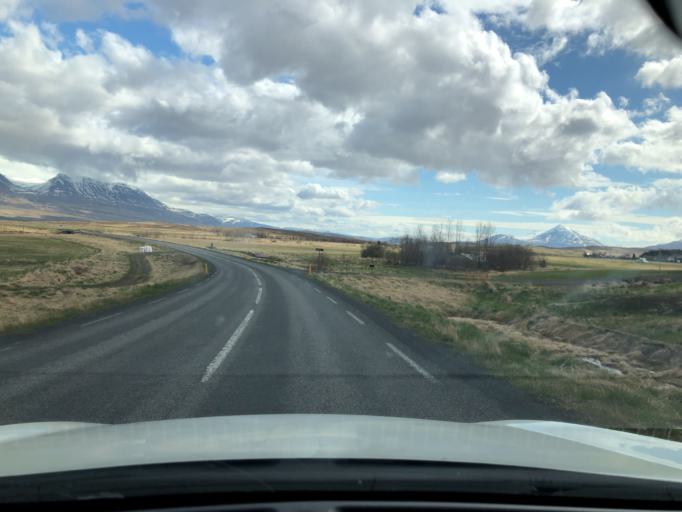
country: IS
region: Northwest
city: Saudarkrokur
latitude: 65.5456
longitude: -19.4734
